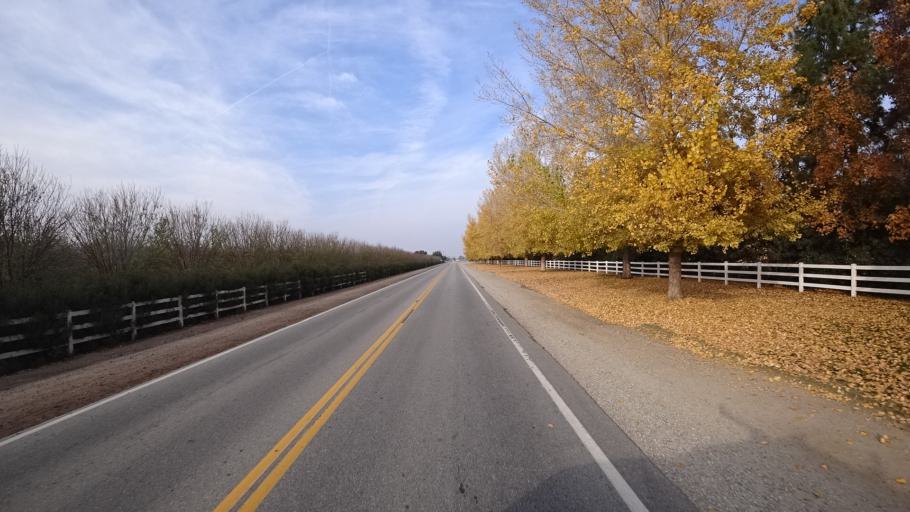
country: US
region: California
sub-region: Kern County
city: Greenacres
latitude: 35.2909
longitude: -119.1282
